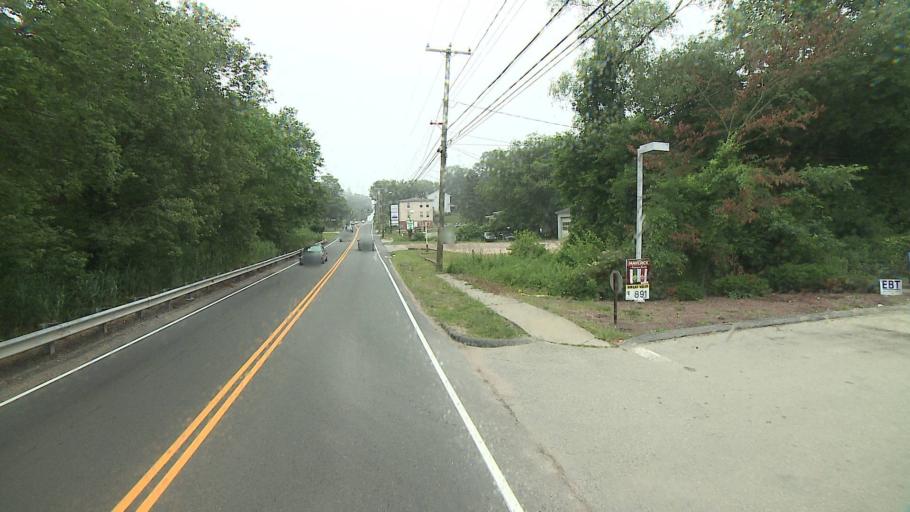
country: US
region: Connecticut
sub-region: New London County
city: Pawcatuck
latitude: 41.3740
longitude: -71.8493
